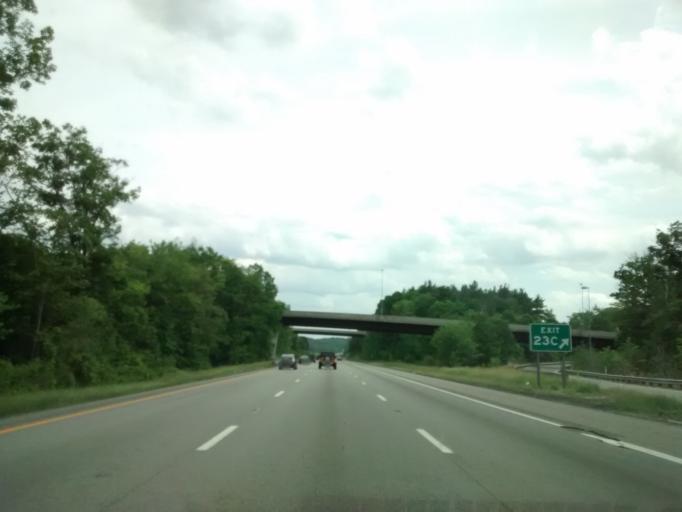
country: US
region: Massachusetts
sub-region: Middlesex County
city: Marlborough
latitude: 42.3238
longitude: -71.5728
